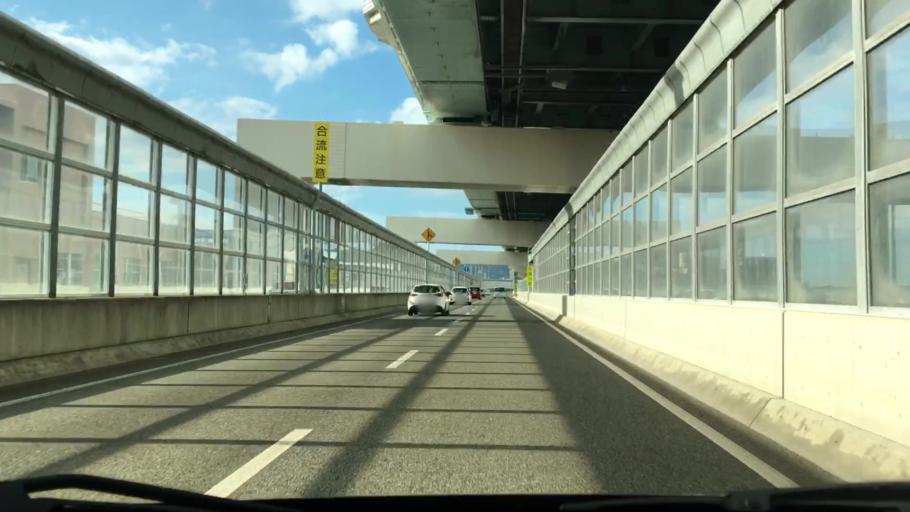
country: JP
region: Fukuoka
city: Fukuoka-shi
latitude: 33.5731
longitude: 130.3164
